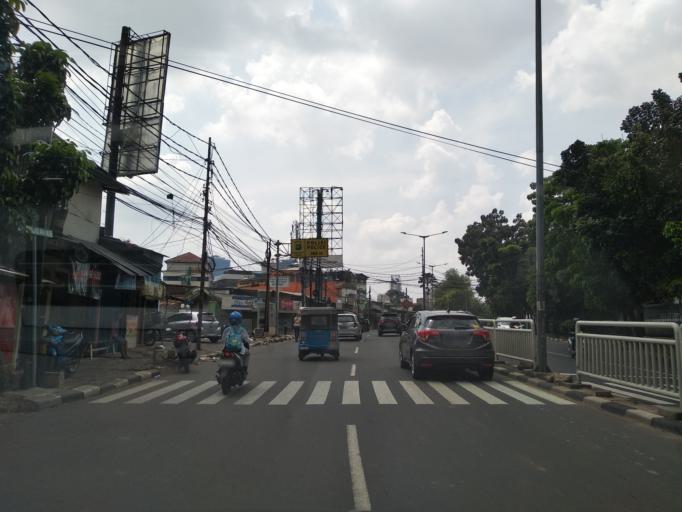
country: ID
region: Jakarta Raya
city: Jakarta
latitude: -6.2345
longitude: 106.8444
